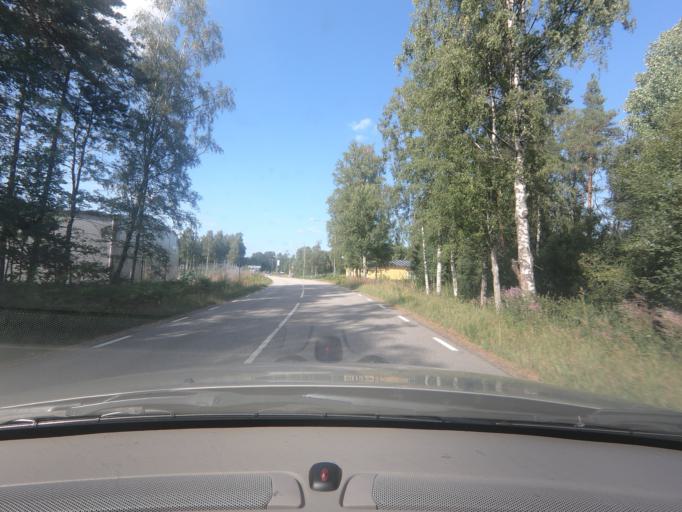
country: SE
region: Joenkoeping
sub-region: Vetlanda Kommun
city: Landsbro
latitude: 57.3635
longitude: 14.9056
